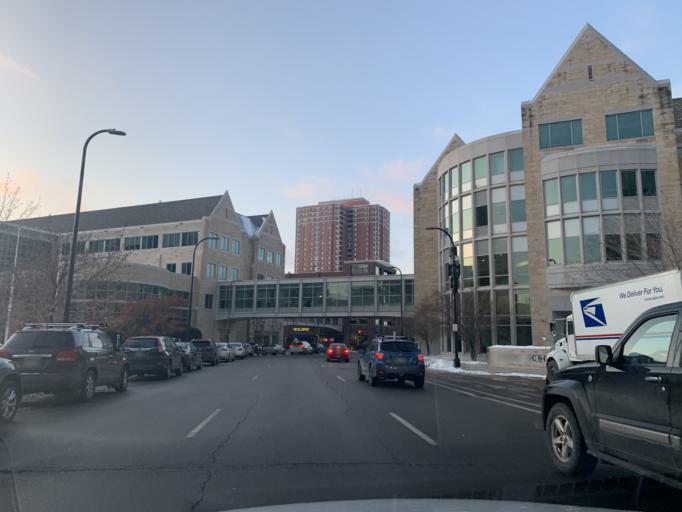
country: US
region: Minnesota
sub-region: Hennepin County
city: Minneapolis
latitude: 44.9738
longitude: -93.2774
